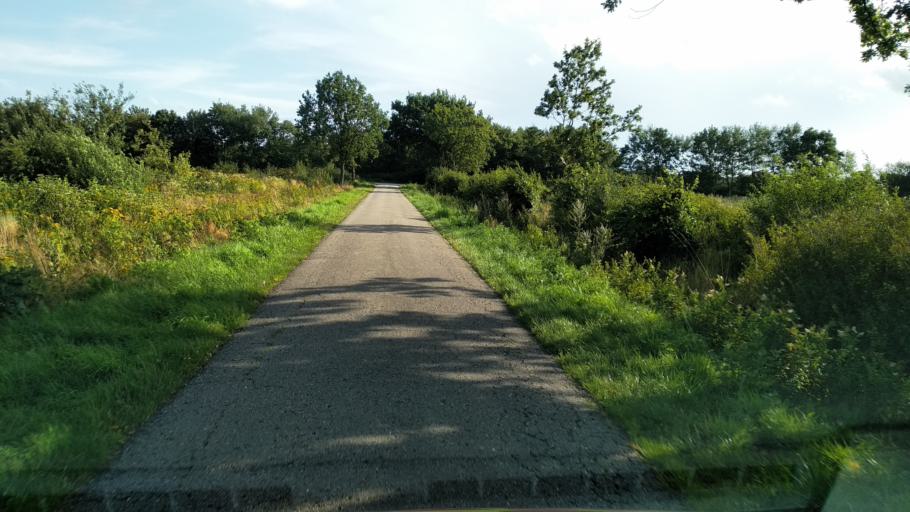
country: DE
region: Schleswig-Holstein
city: Gross Rheide
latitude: 54.4282
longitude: 9.4282
